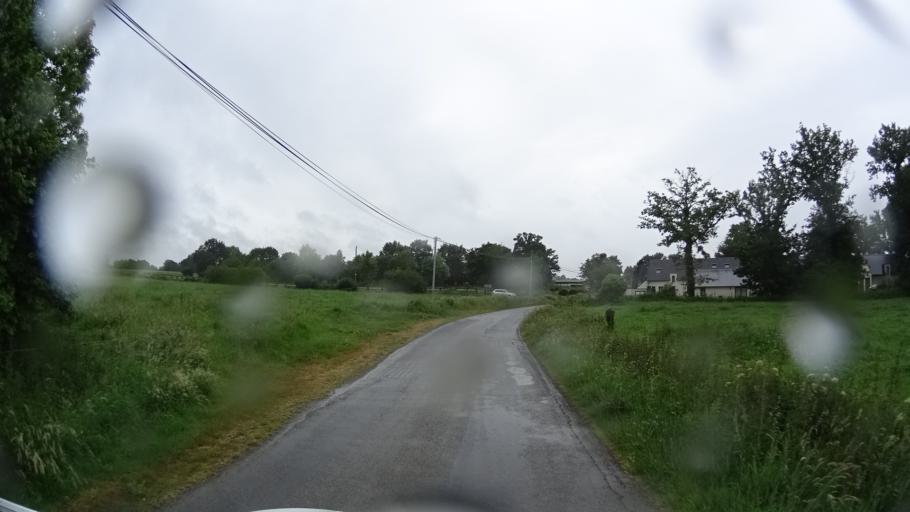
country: FR
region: Brittany
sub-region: Departement d'Ille-et-Vilaine
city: Saint-Erblon
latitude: 48.0265
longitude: -1.6282
